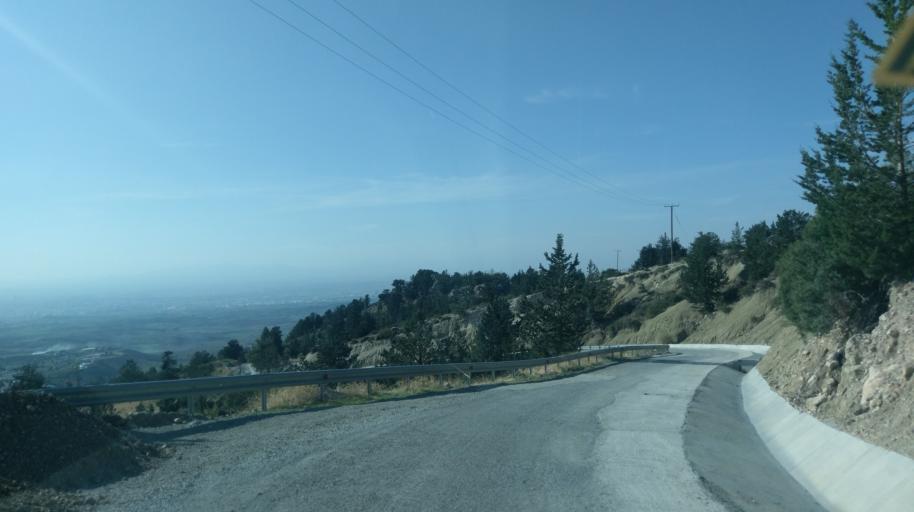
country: CY
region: Keryneia
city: Kyrenia
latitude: 35.2831
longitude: 33.3868
